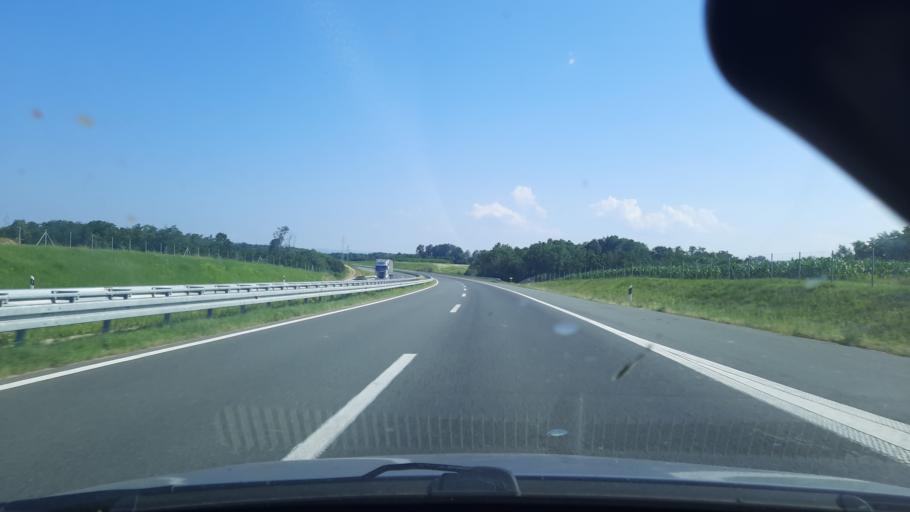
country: RS
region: Central Serbia
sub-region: Kolubarski Okrug
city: Ub
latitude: 44.4024
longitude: 20.0944
